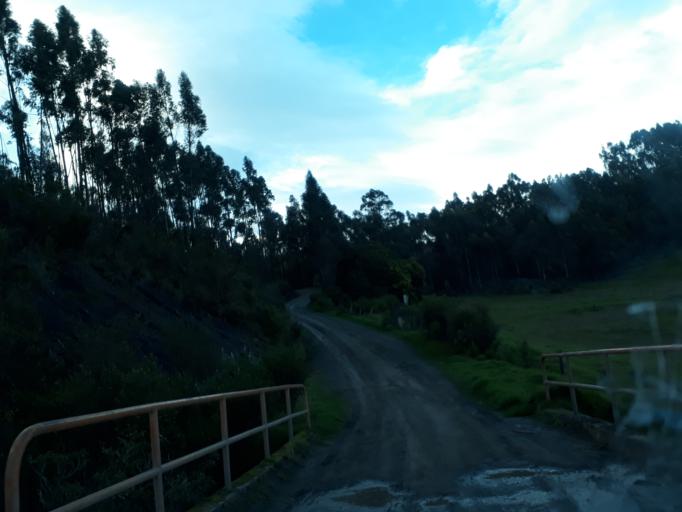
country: CO
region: Cundinamarca
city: Carmen de Carupa
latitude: 5.3392
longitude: -73.9062
